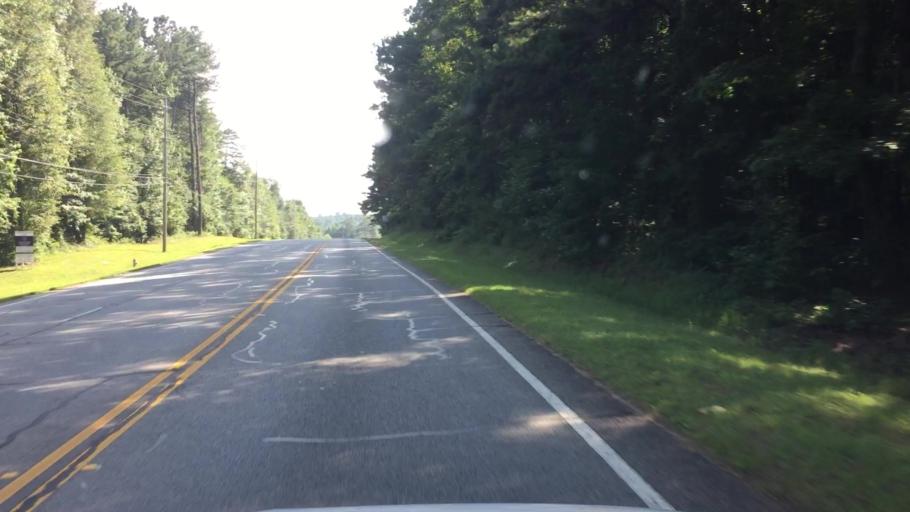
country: US
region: Georgia
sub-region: Barrow County
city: Auburn
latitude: 34.0083
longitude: -83.8567
